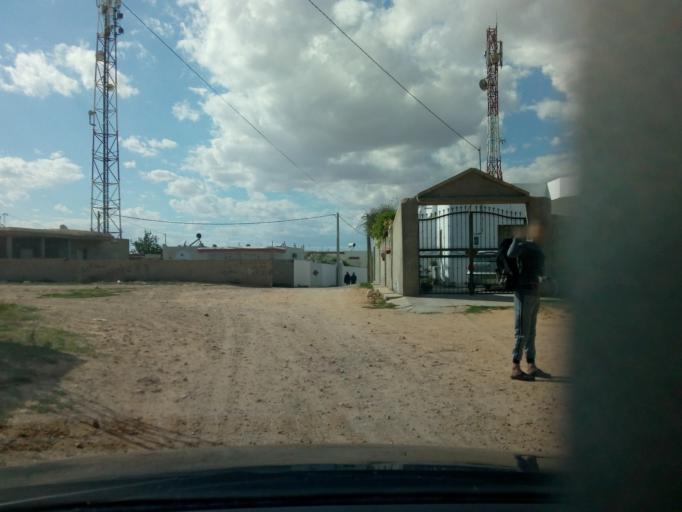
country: TN
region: Safaqis
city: Sfax
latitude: 34.7267
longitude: 10.6079
